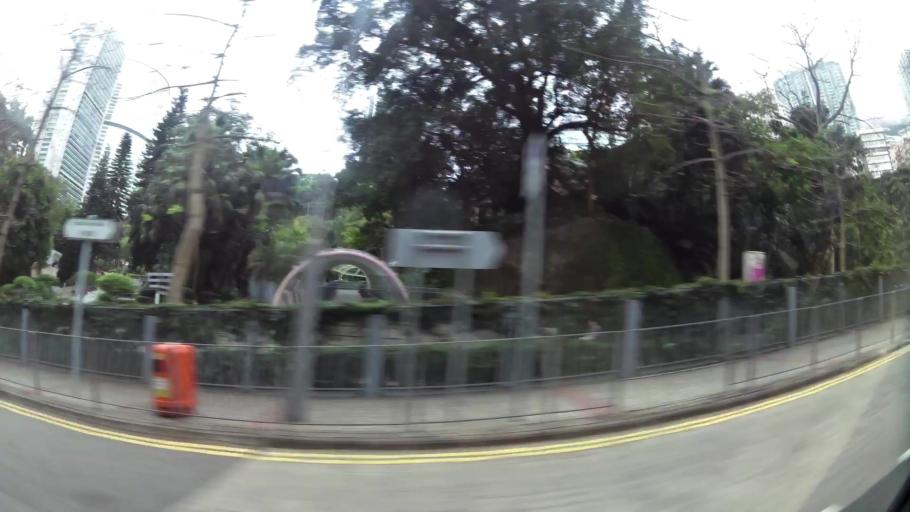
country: HK
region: Central and Western
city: Central
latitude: 22.2778
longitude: 114.1607
